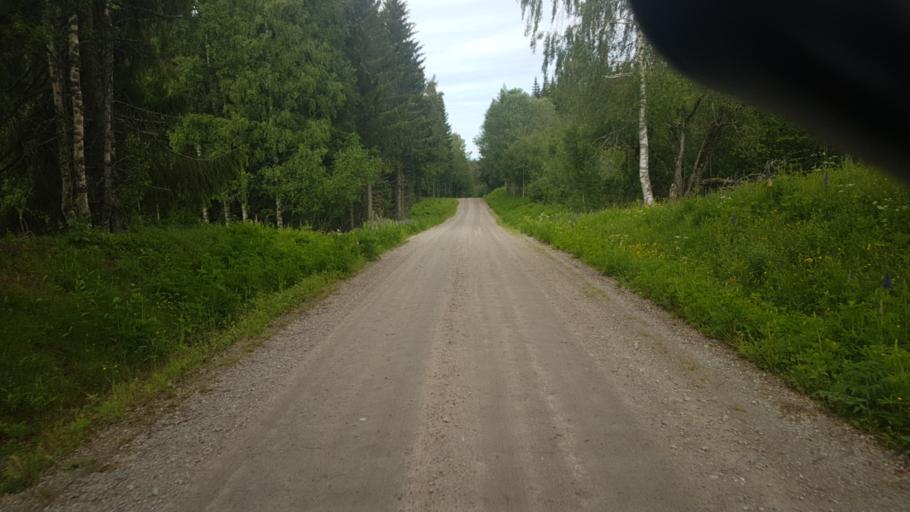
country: SE
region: Vaermland
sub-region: Arvika Kommun
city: Arvika
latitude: 59.8380
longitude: 12.8032
